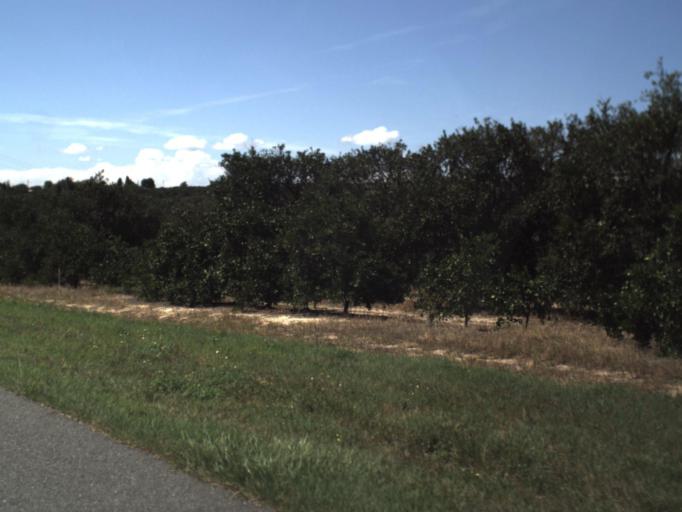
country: US
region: Florida
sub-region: Polk County
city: Dundee
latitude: 27.9839
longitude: -81.5949
